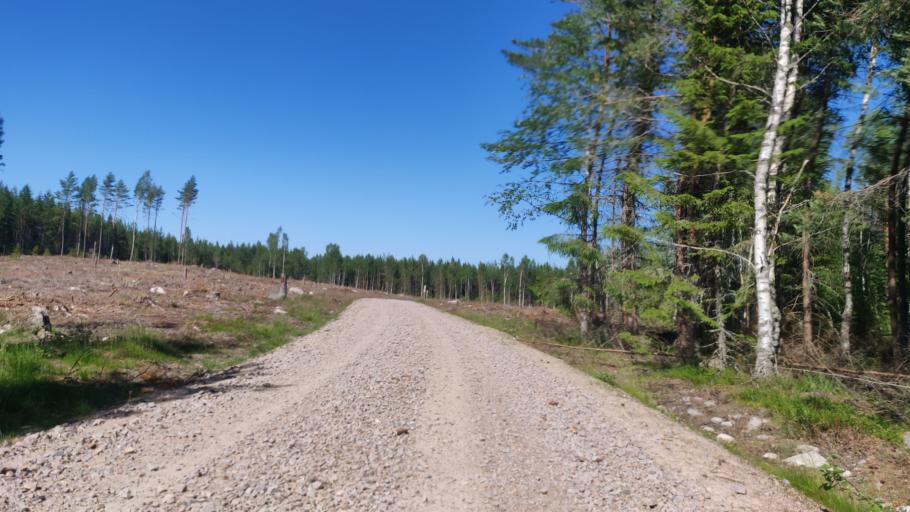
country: SE
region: Vaermland
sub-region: Hagfors Kommun
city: Hagfors
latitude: 59.9823
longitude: 13.5983
